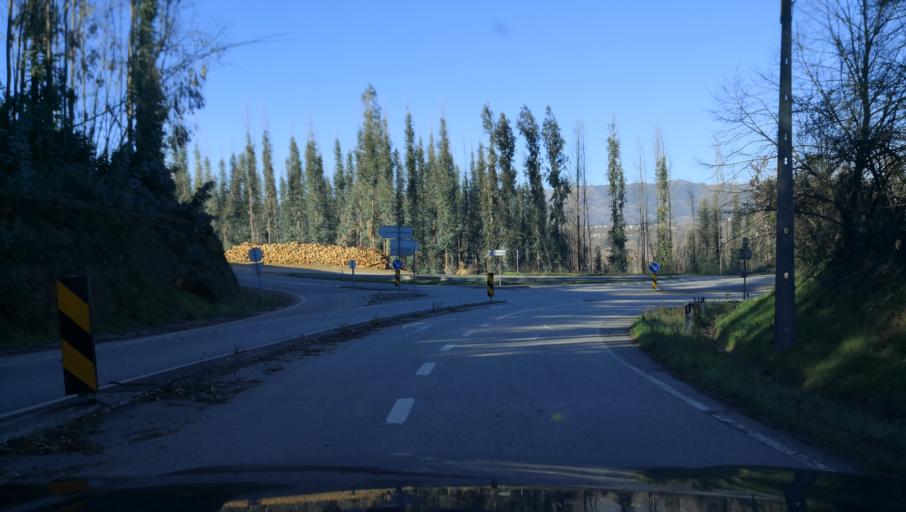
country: PT
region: Viseu
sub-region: Vouzela
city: Vouzela
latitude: 40.7276
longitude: -8.1257
